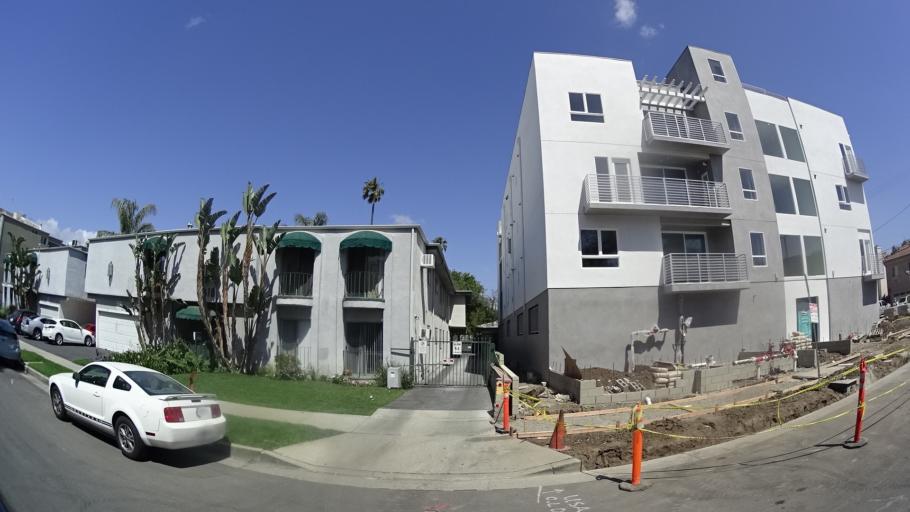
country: US
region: California
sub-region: Los Angeles County
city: Sherman Oaks
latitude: 34.1534
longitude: -118.4367
